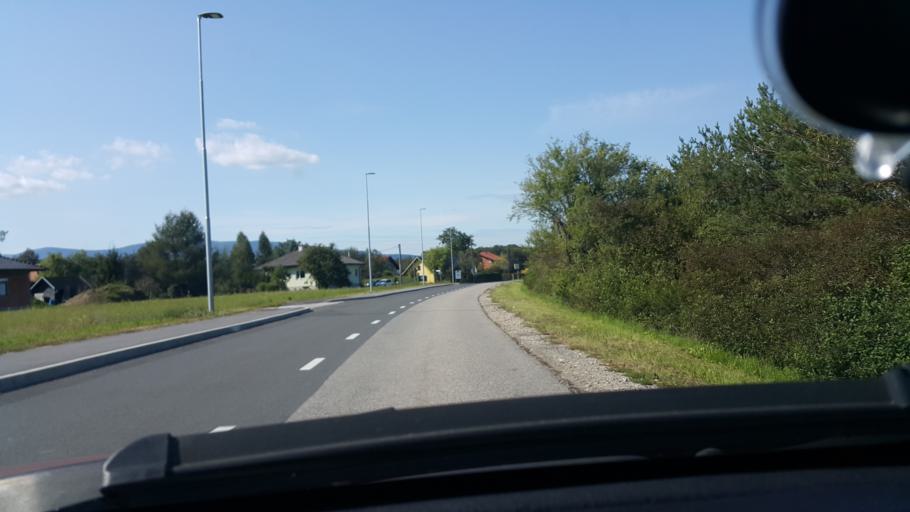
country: SI
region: Race-Fram
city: Race
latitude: 46.4666
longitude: 15.7146
